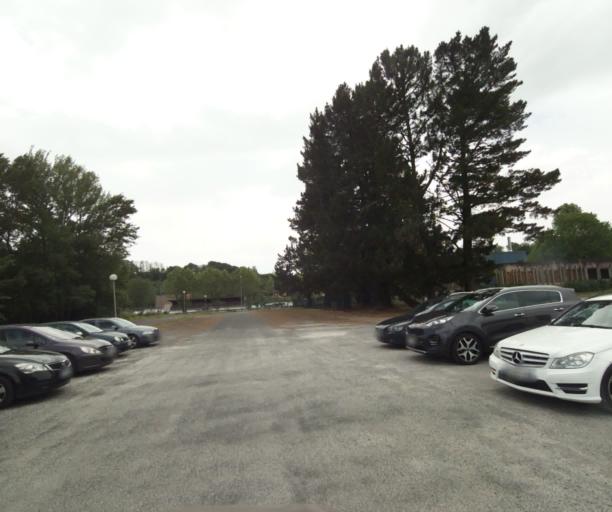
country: FR
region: Aquitaine
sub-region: Departement des Pyrenees-Atlantiques
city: Mouguerre
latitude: 43.4863
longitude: -1.4300
